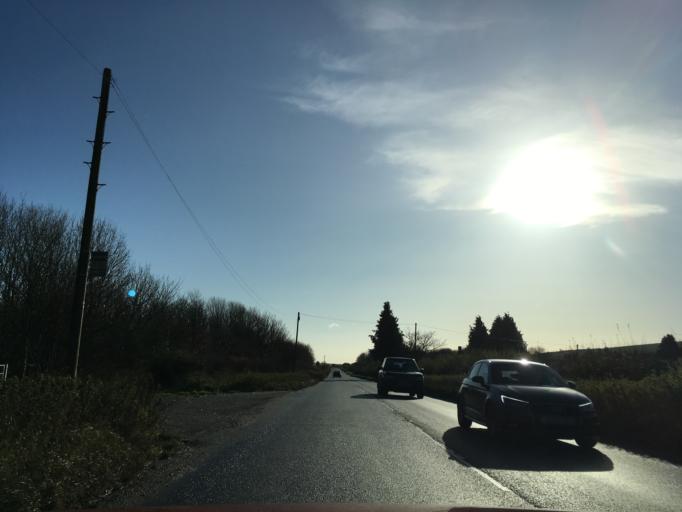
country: GB
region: England
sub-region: Wiltshire
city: Collingbourne Kingston
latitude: 51.3238
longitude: -1.6750
